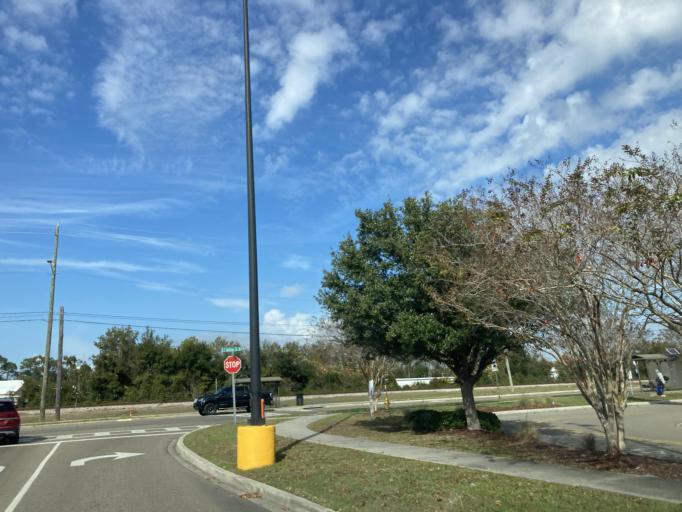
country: US
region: Mississippi
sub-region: Harrison County
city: West Gulfport
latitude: 30.3939
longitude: -88.9961
